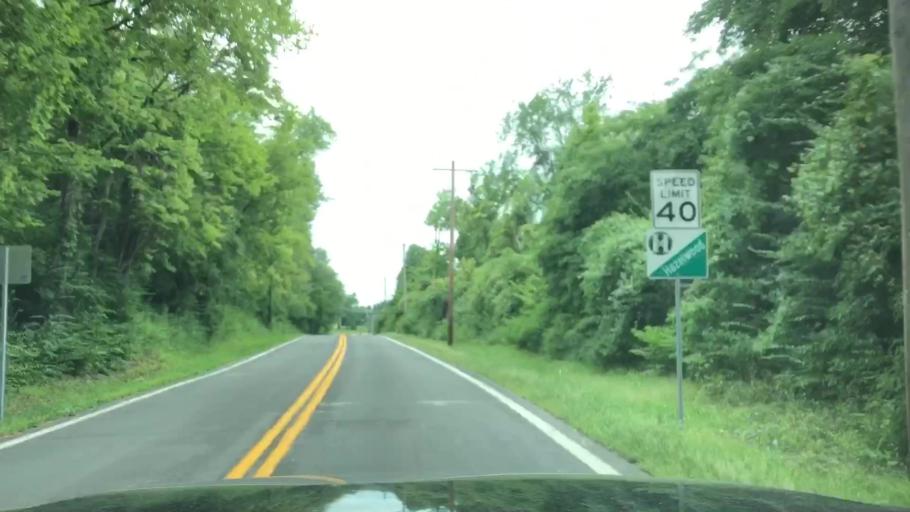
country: US
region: Missouri
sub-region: Saint Louis County
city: Hazelwood
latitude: 38.8130
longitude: -90.3789
